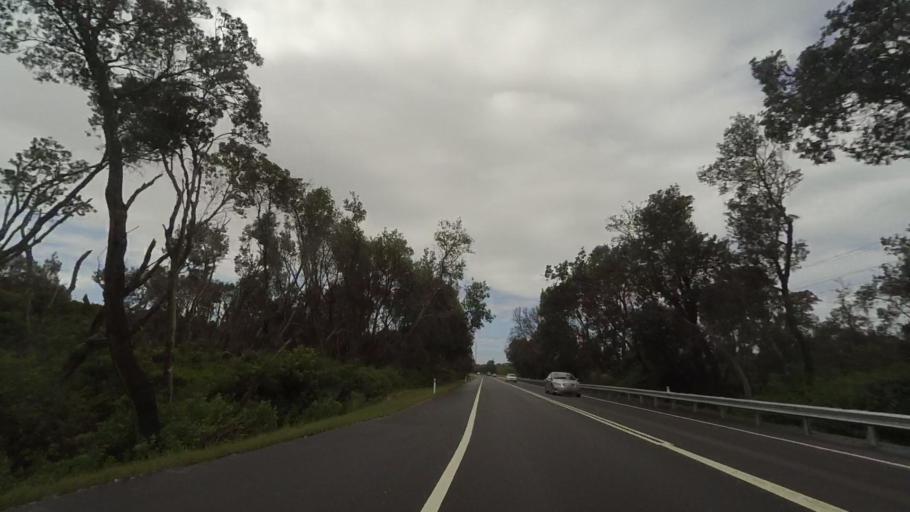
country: AU
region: New South Wales
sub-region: Wyong Shire
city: The Entrance
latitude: -33.3192
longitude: 151.5165
